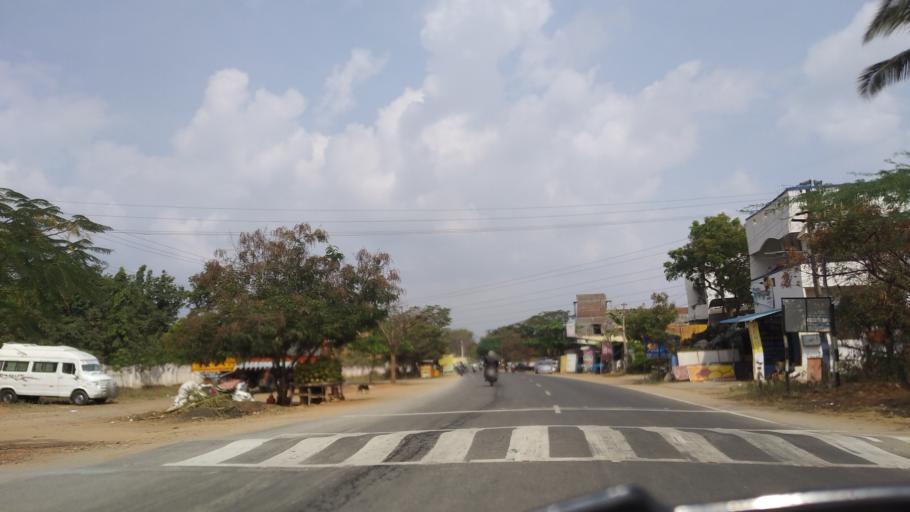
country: IN
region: Tamil Nadu
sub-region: Coimbatore
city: Madukkarai
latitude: 10.9402
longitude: 76.9433
